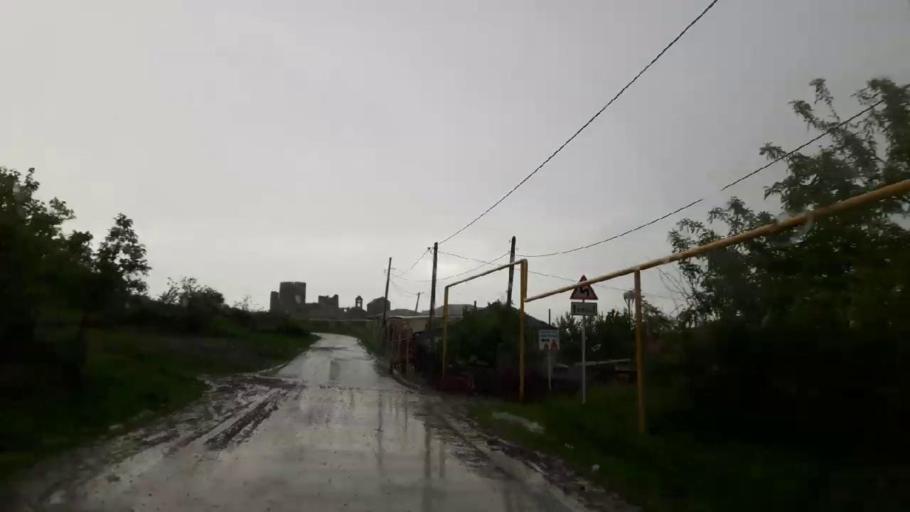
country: GE
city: Agara
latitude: 42.0169
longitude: 43.8371
